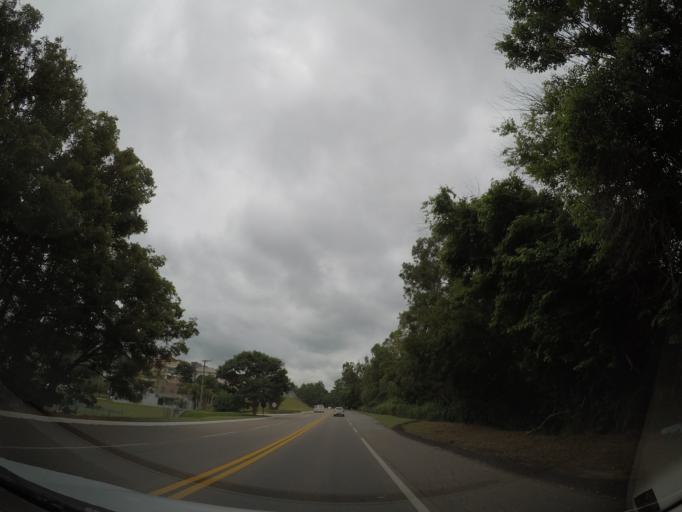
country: BR
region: Sao Paulo
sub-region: Louveira
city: Louveira
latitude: -23.0672
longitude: -46.9500
